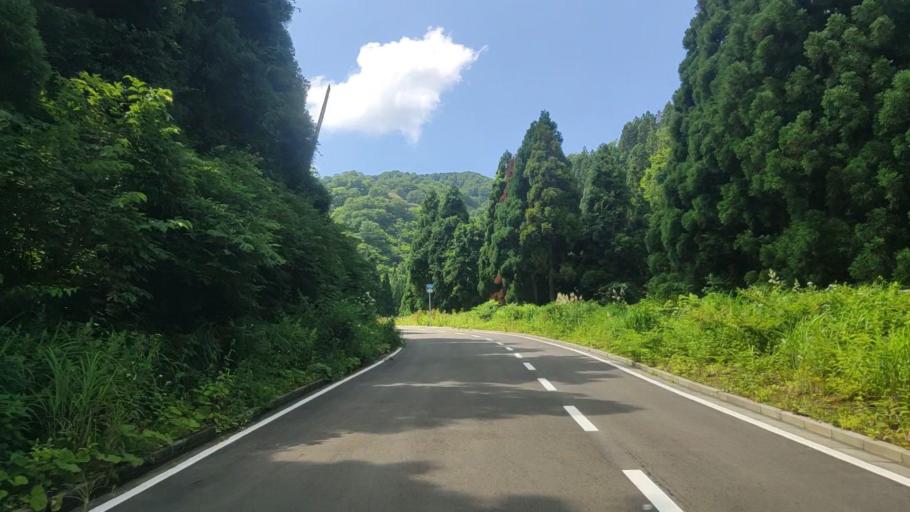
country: JP
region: Fukui
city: Katsuyama
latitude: 36.1569
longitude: 136.5264
